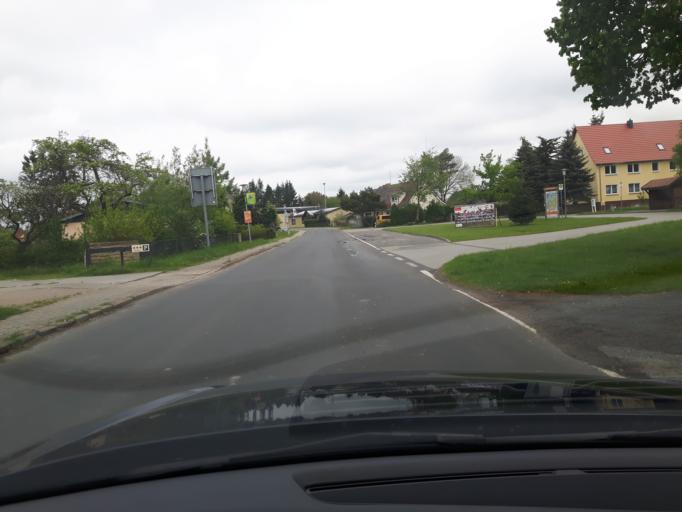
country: DE
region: Mecklenburg-Vorpommern
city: Tribsees
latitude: 54.1622
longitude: 12.7245
